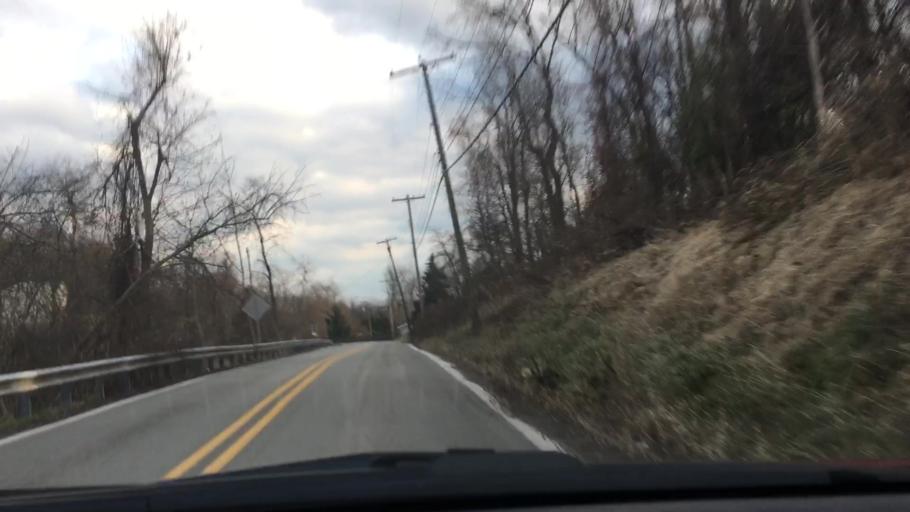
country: US
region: Pennsylvania
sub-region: Allegheny County
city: Lincoln
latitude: 40.2998
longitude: -79.8518
